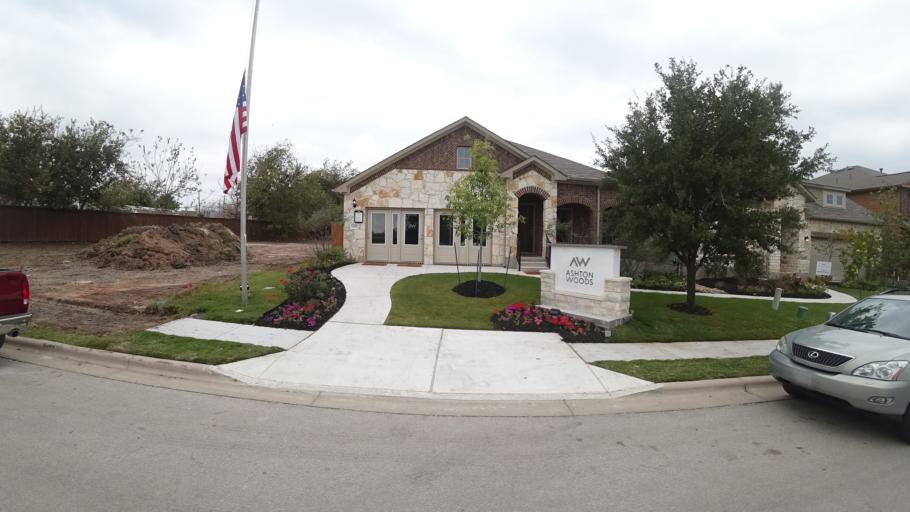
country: US
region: Texas
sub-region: Travis County
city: Pflugerville
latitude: 30.3890
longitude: -97.6198
